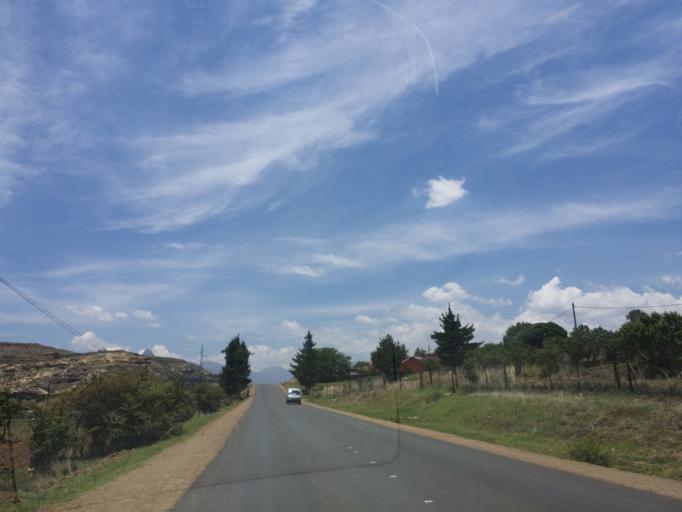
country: LS
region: Butha-Buthe
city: Butha-Buthe
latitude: -28.7334
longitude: 28.4049
